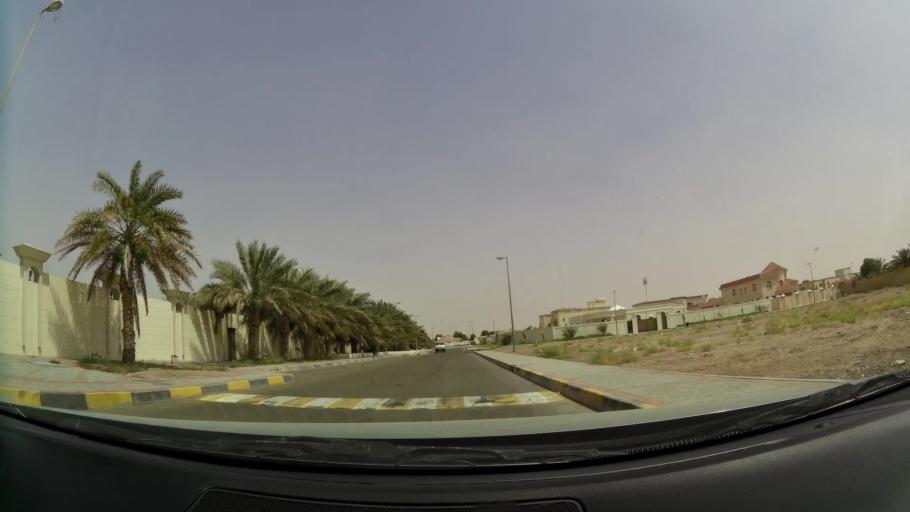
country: AE
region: Abu Dhabi
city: Al Ain
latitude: 24.1434
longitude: 55.6417
